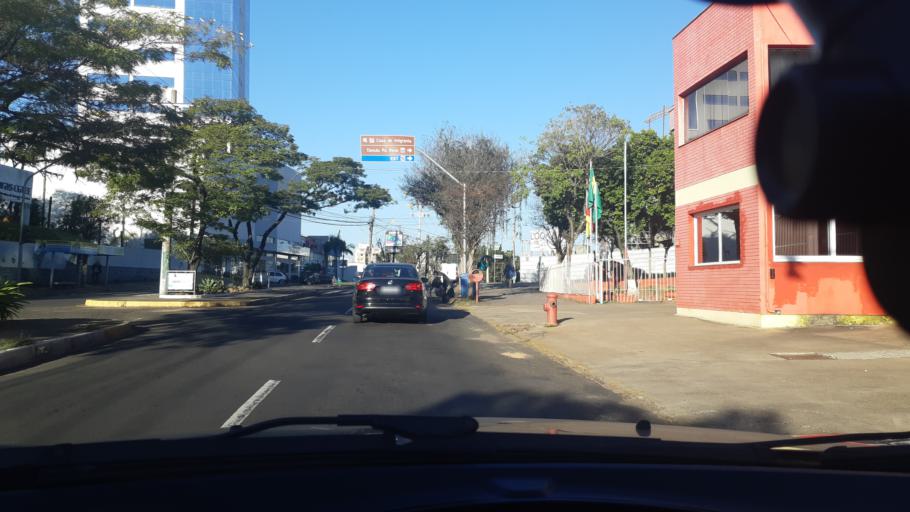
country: BR
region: Rio Grande do Sul
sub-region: Sao Leopoldo
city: Sao Leopoldo
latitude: -29.7695
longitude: -51.1364
